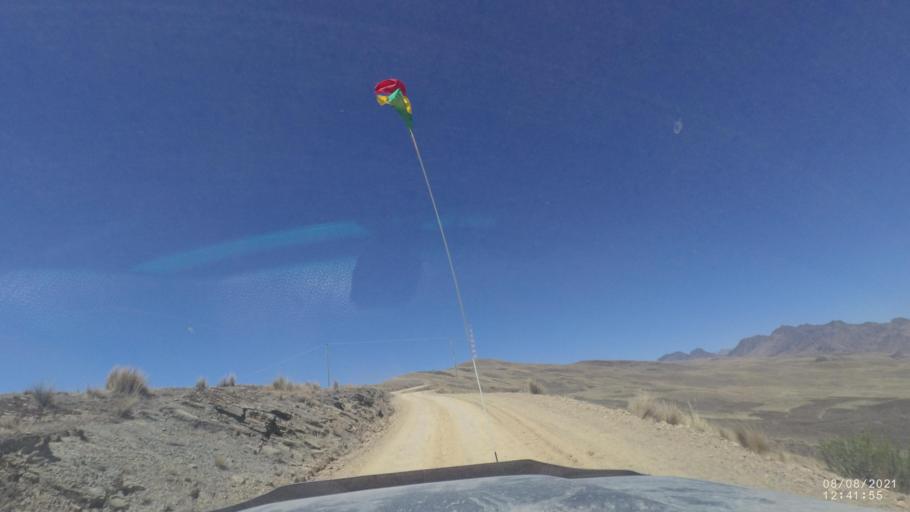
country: BO
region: Cochabamba
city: Colchani
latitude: -16.8366
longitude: -66.6182
